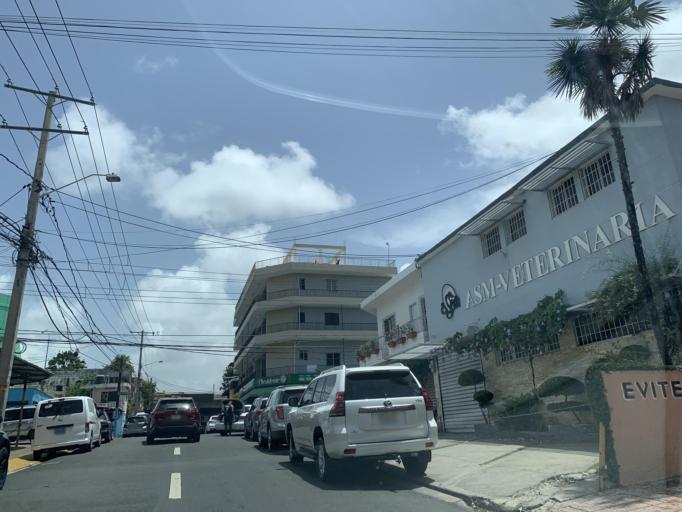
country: DO
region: Nacional
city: San Carlos
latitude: 18.4766
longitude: -69.9030
